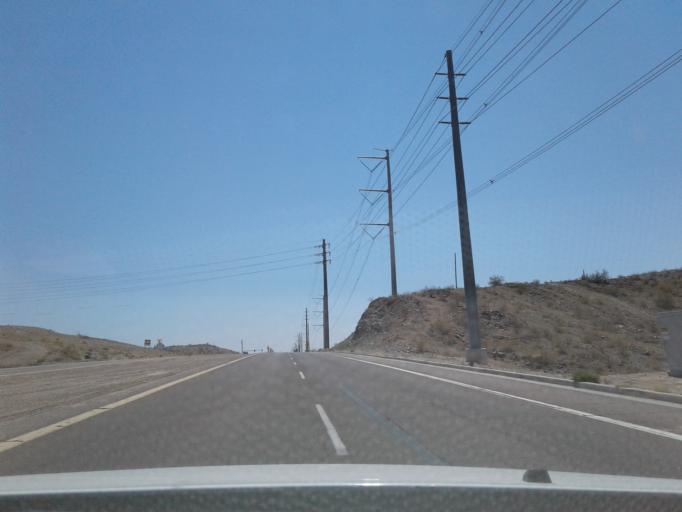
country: US
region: Arizona
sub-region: Maricopa County
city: Laveen
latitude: 33.2909
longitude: -112.0683
